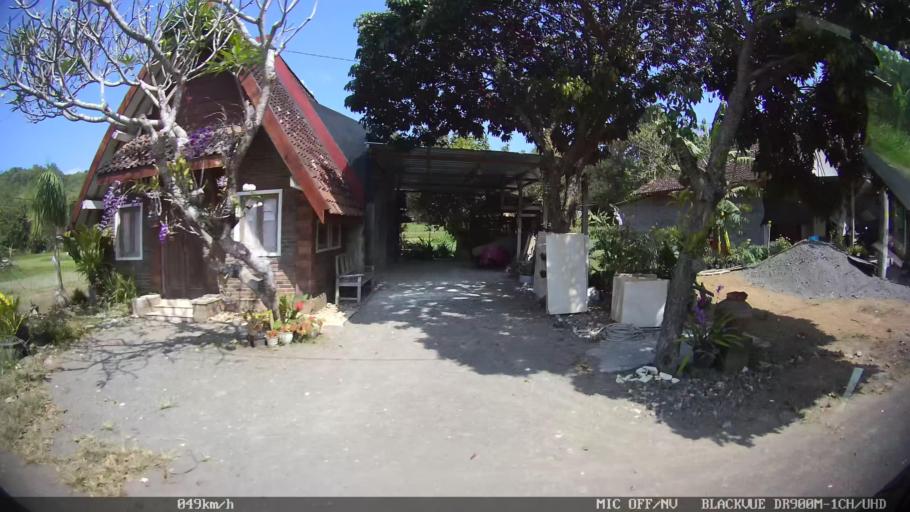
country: ID
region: Daerah Istimewa Yogyakarta
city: Pundong
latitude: -7.9894
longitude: 110.3178
